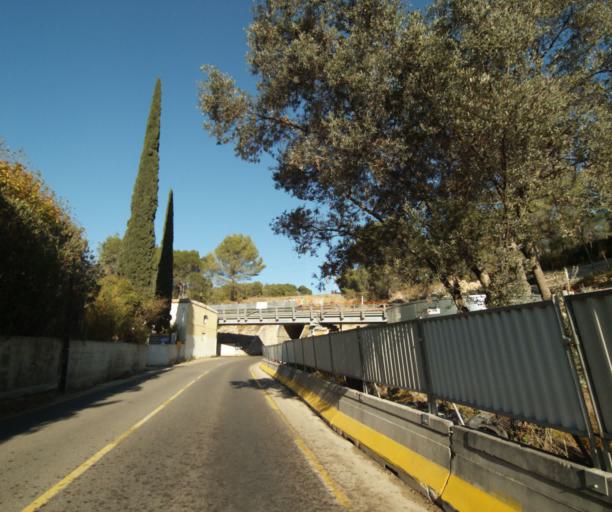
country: FR
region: Provence-Alpes-Cote d'Azur
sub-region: Departement des Bouches-du-Rhone
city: La Ciotat
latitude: 43.2017
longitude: 5.5882
